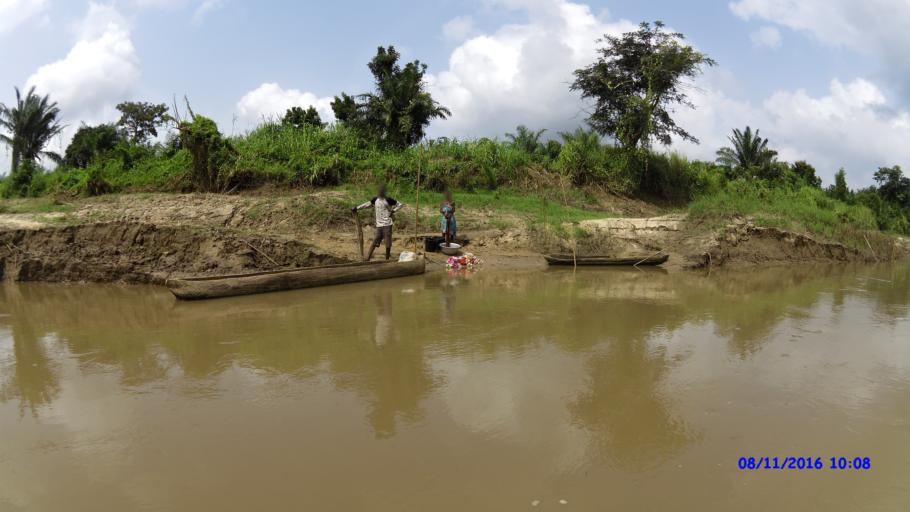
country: BJ
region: Mono
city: Come
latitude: 6.4512
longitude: 1.7535
